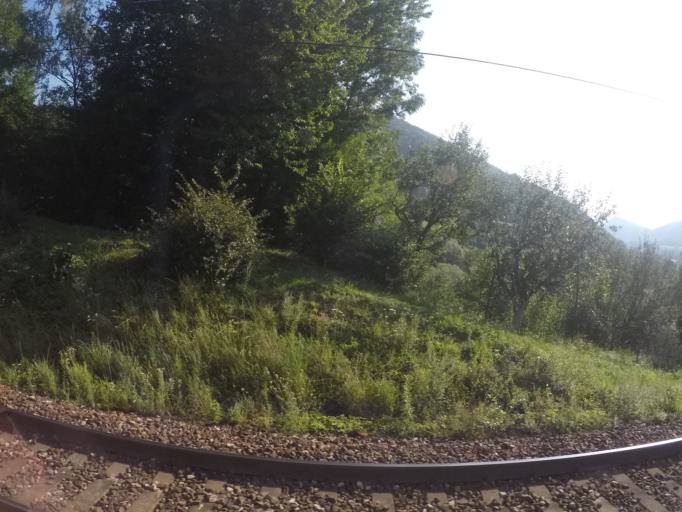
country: SK
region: Presovsky
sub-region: Okres Presov
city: Presov
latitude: 48.8551
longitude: 21.1569
